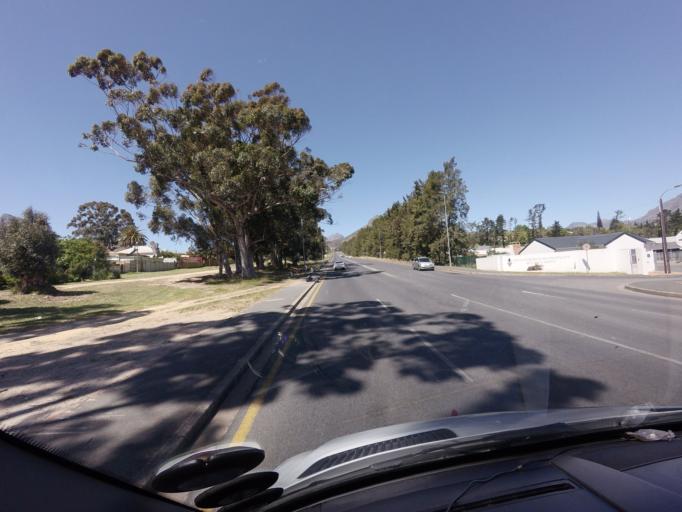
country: ZA
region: Western Cape
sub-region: Cape Winelands District Municipality
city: Stellenbosch
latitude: -33.9255
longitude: 18.8822
